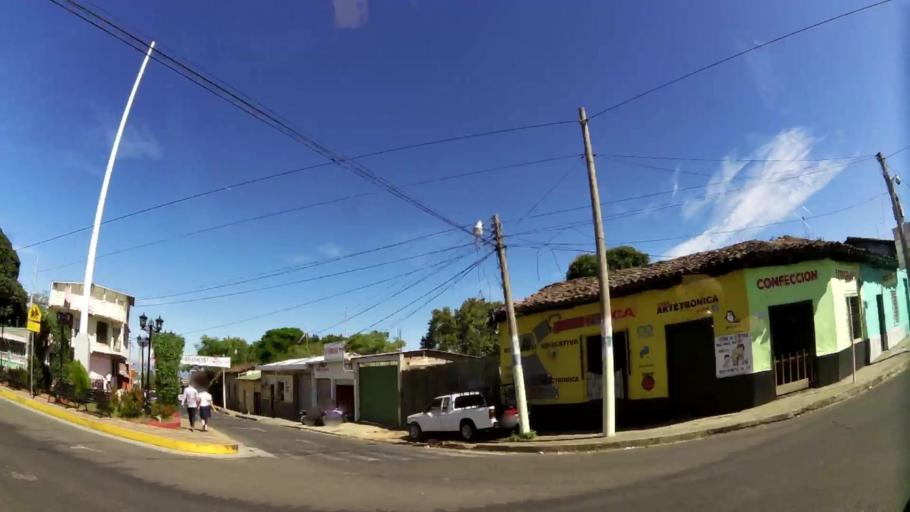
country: SV
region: Ahuachapan
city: Ahuachapan
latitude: 13.9245
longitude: -89.8497
